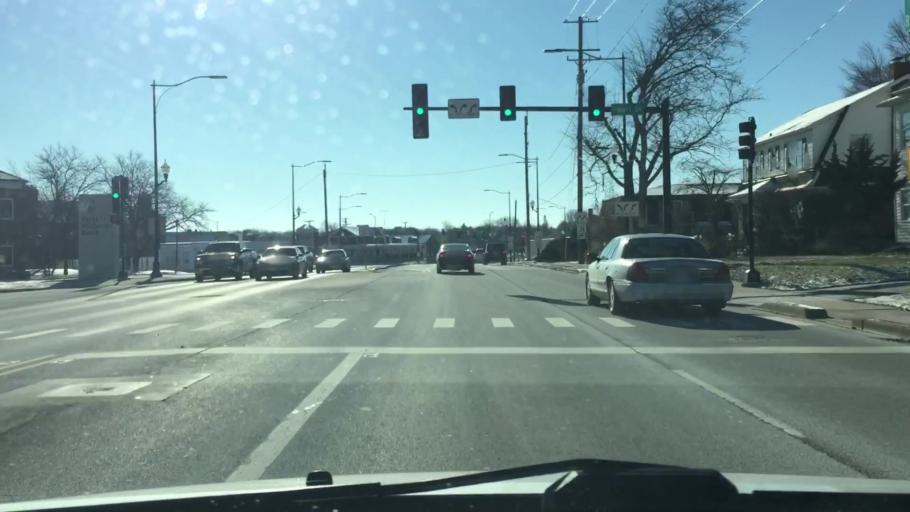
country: US
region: Illinois
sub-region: McHenry County
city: McHenry
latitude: 42.3476
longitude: -88.2674
